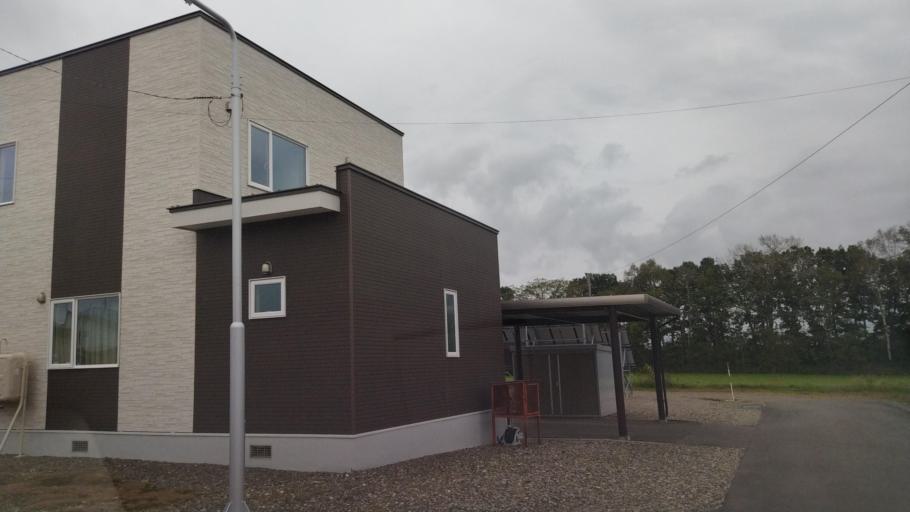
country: JP
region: Hokkaido
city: Otofuke
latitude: 43.2304
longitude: 143.2848
